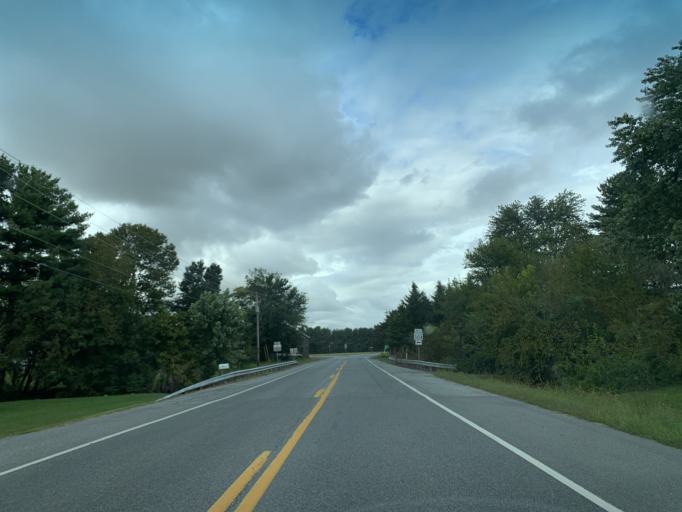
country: US
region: Maryland
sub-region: Caroline County
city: Ridgely
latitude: 39.0333
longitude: -75.8747
